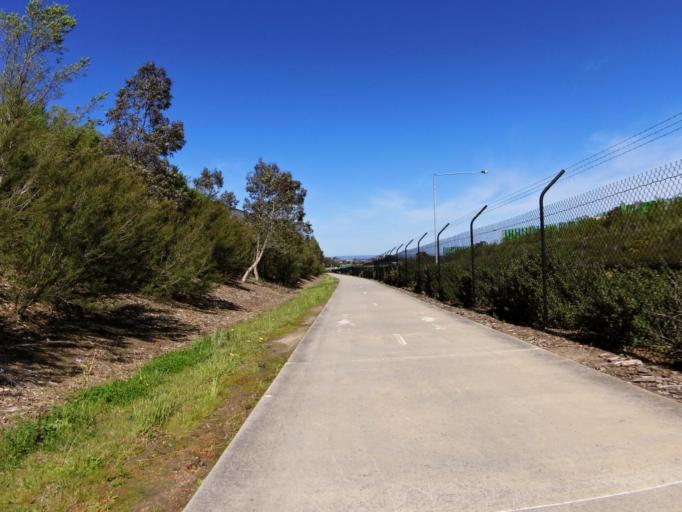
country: AU
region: Victoria
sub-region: Greater Dandenong
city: Noble Park North
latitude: -37.9521
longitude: 145.2040
